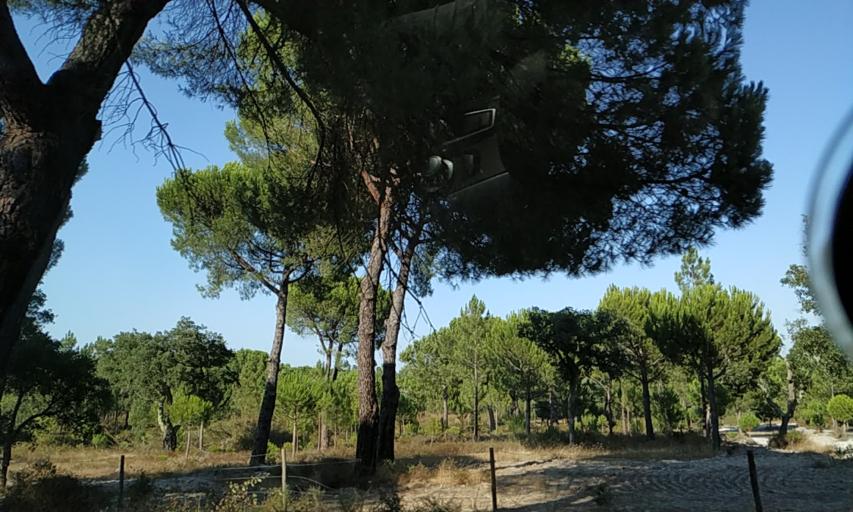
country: PT
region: Santarem
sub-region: Coruche
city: Coruche
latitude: 38.9806
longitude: -8.5457
